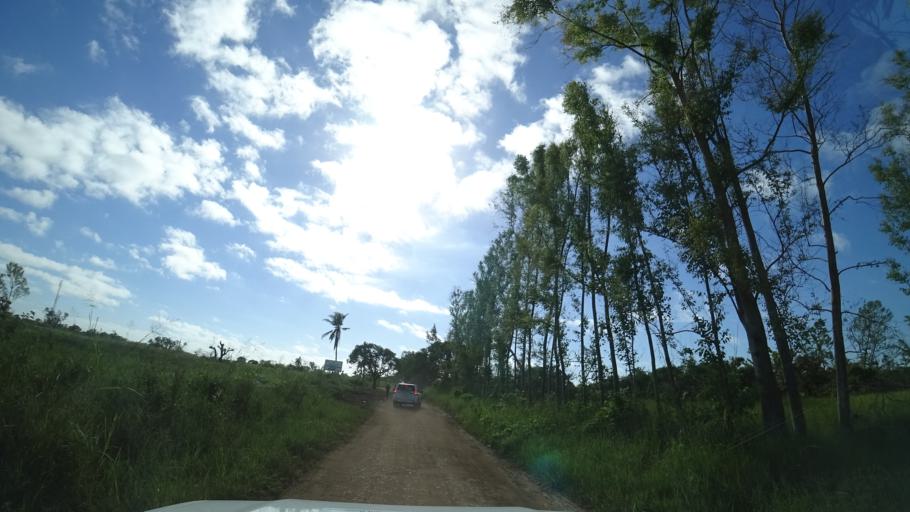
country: MZ
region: Sofala
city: Beira
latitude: -19.7187
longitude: 35.0029
